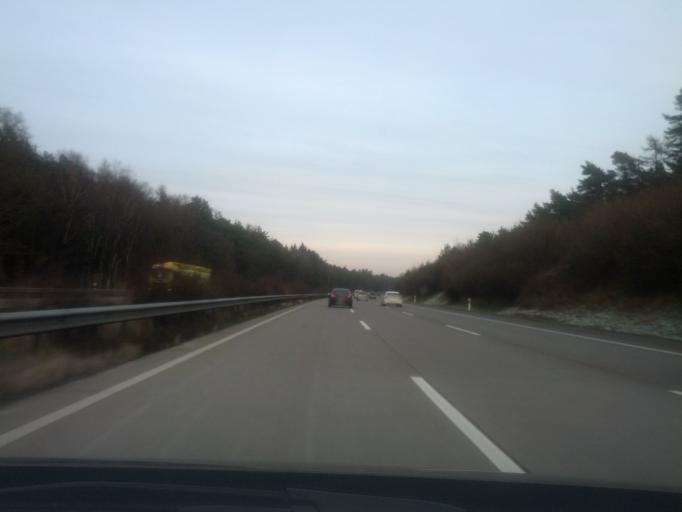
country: DE
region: Lower Saxony
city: Bispingen
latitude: 53.1376
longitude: 9.9997
